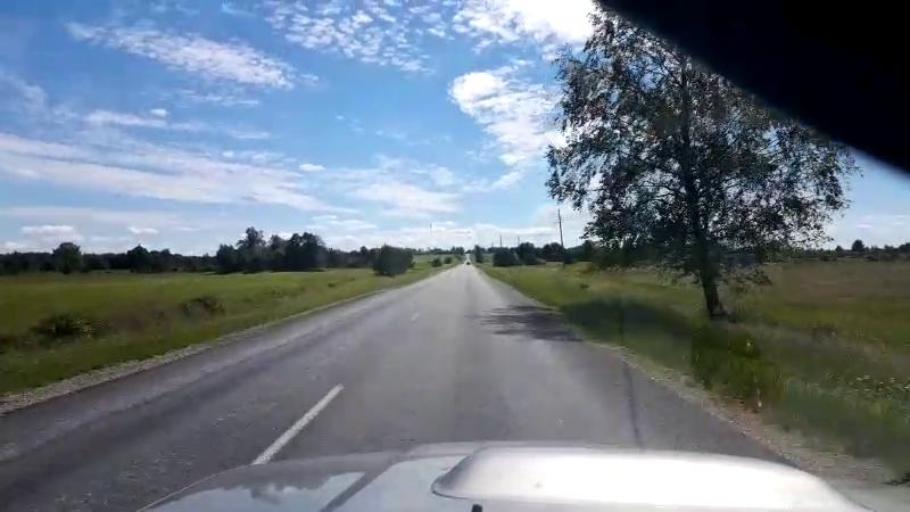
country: EE
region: Laeaene-Virumaa
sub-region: Rakke vald
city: Rakke
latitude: 58.8645
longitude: 26.2940
